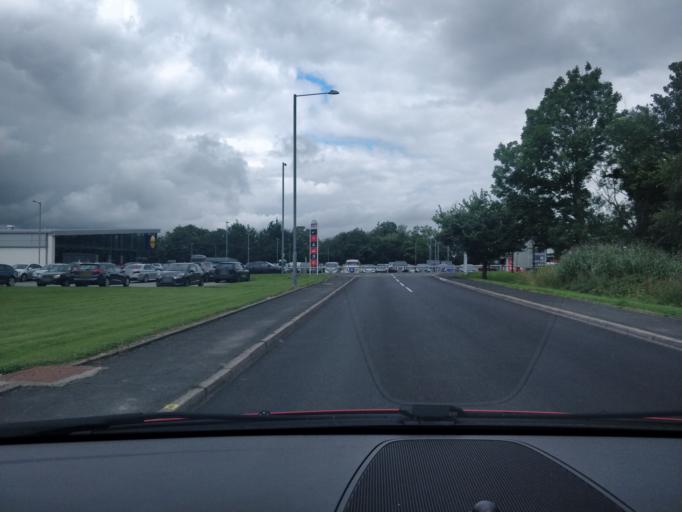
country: GB
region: Wales
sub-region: Gwynedd
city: Porthmadog
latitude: 52.9288
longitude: -4.1394
